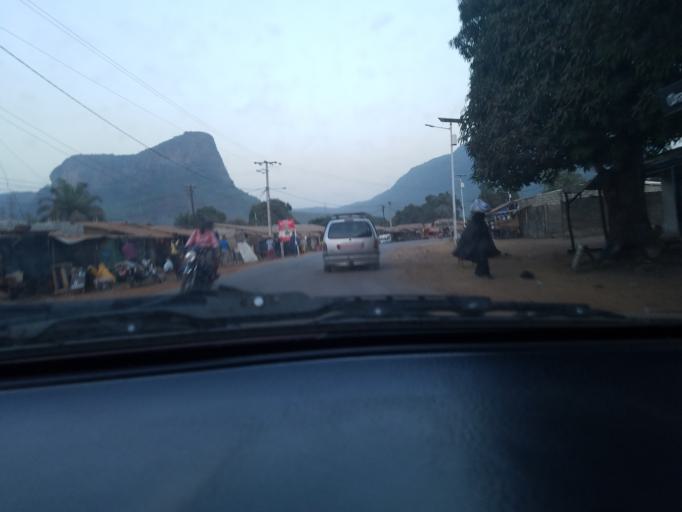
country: GN
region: Kindia
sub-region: Prefecture de Dubreka
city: Dubreka
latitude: 9.7901
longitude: -13.4905
